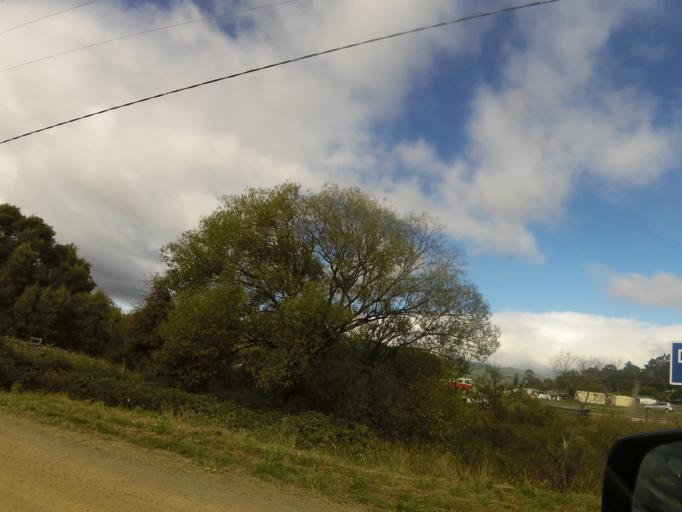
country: AU
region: Tasmania
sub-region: Huon Valley
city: Huonville
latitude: -43.0042
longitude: 147.0420
